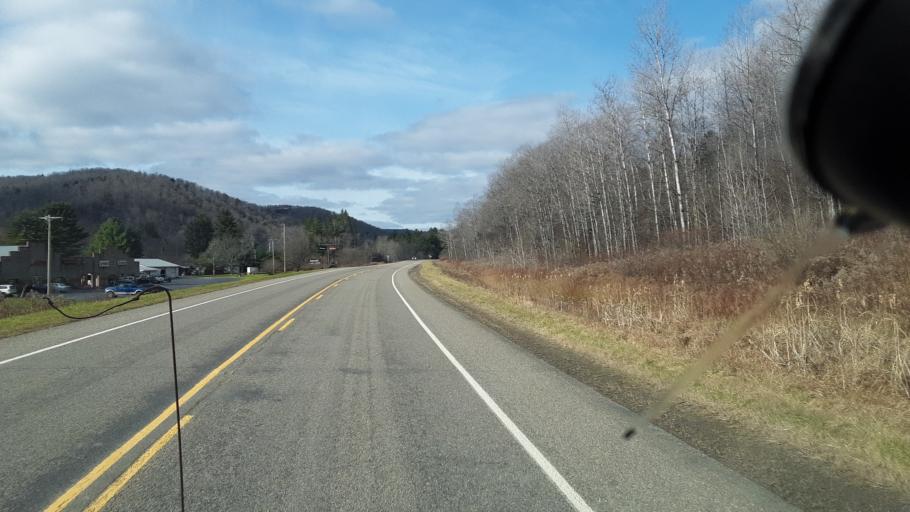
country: US
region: Pennsylvania
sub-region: Potter County
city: Galeton
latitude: 41.7778
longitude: -77.7242
